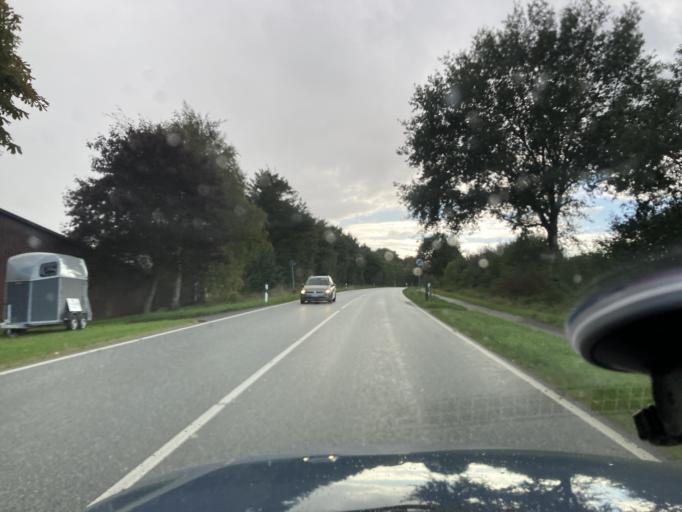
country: DE
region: Schleswig-Holstein
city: Suderdorf
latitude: 54.2187
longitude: 9.3379
